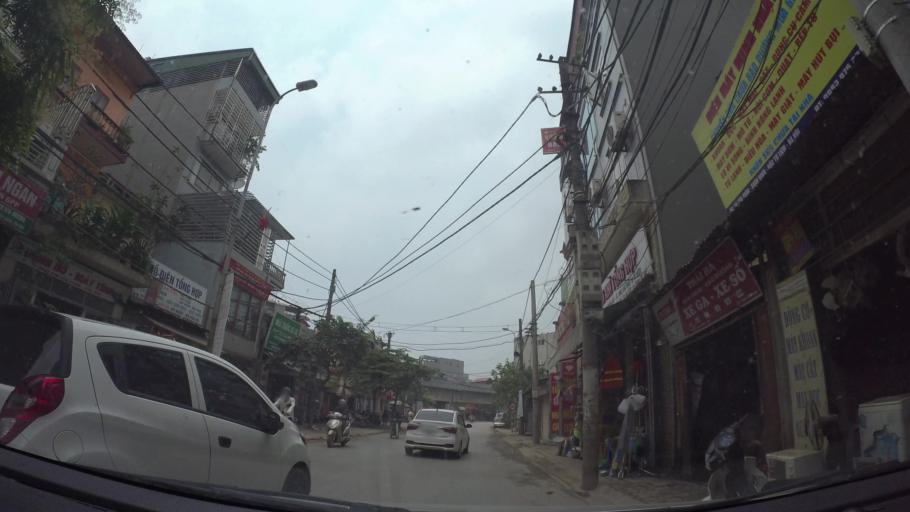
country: VN
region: Ha Noi
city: Tay Ho
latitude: 21.0791
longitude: 105.7862
